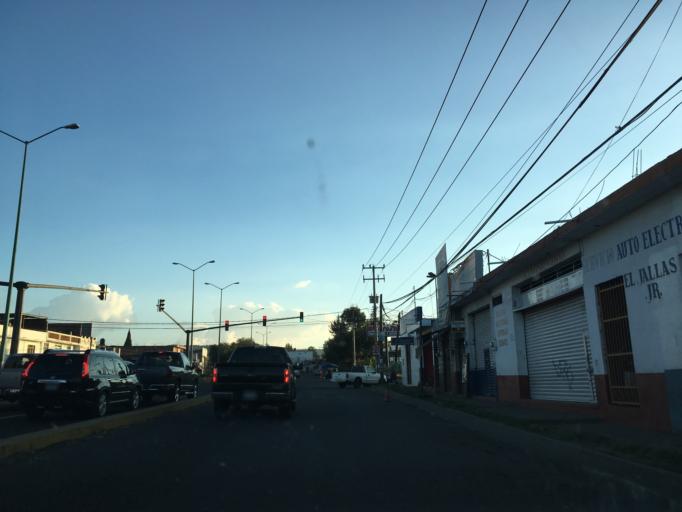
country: MX
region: Michoacan
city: Patzcuaro
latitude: 19.5141
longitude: -101.6186
